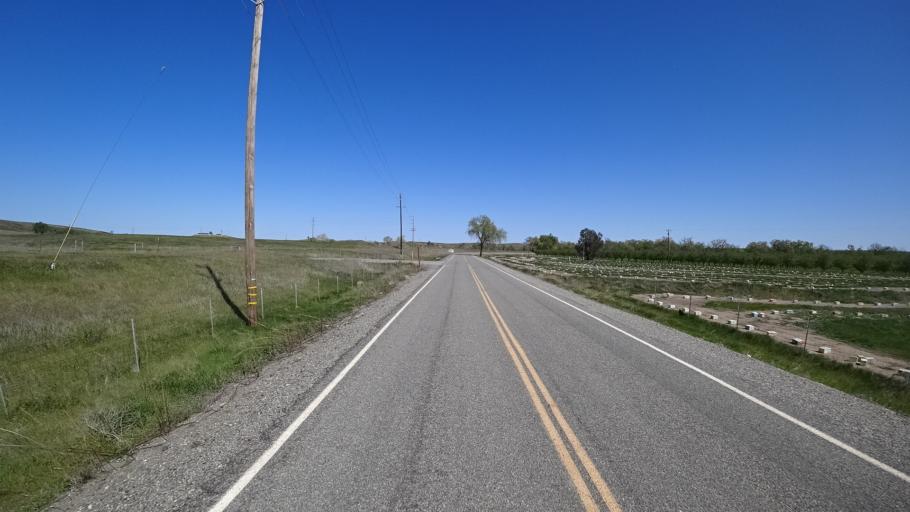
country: US
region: California
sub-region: Glenn County
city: Orland
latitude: 39.8117
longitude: -122.3294
